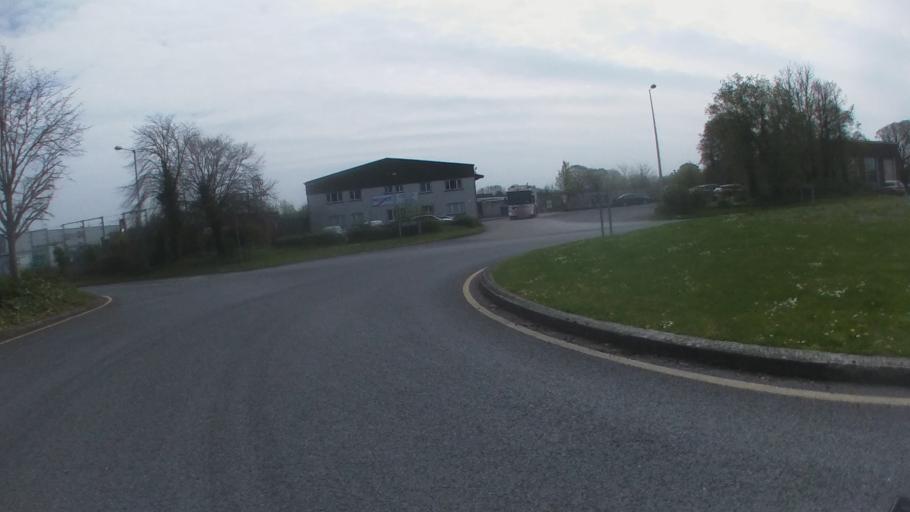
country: IE
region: Leinster
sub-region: Kilkenny
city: Kilkenny
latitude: 52.6441
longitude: -7.2104
